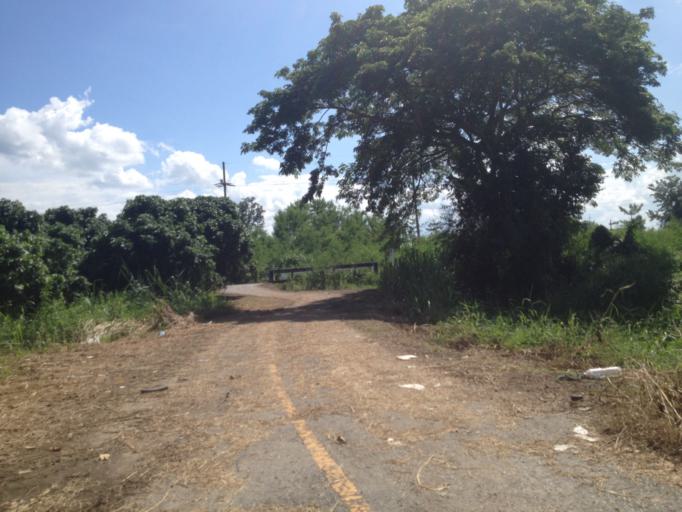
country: TH
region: Chiang Mai
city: Hang Dong
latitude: 18.7012
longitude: 98.9765
